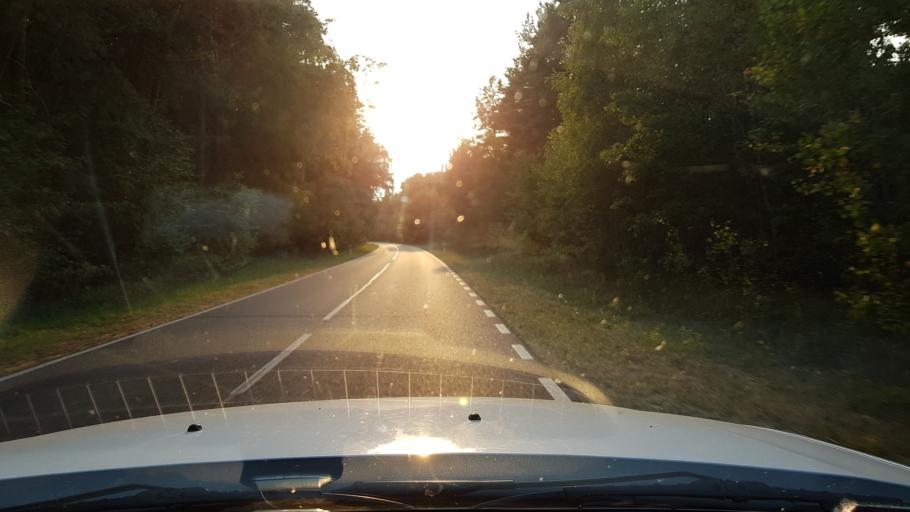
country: PL
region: West Pomeranian Voivodeship
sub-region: Powiat stargardzki
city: Stara Dabrowa
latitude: 53.4339
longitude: 15.2049
